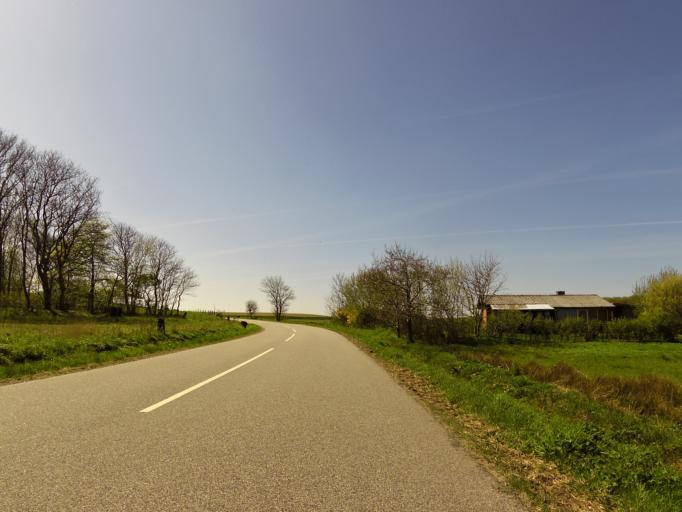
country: DK
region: Central Jutland
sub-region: Struer Kommune
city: Struer
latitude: 56.5173
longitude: 8.5957
